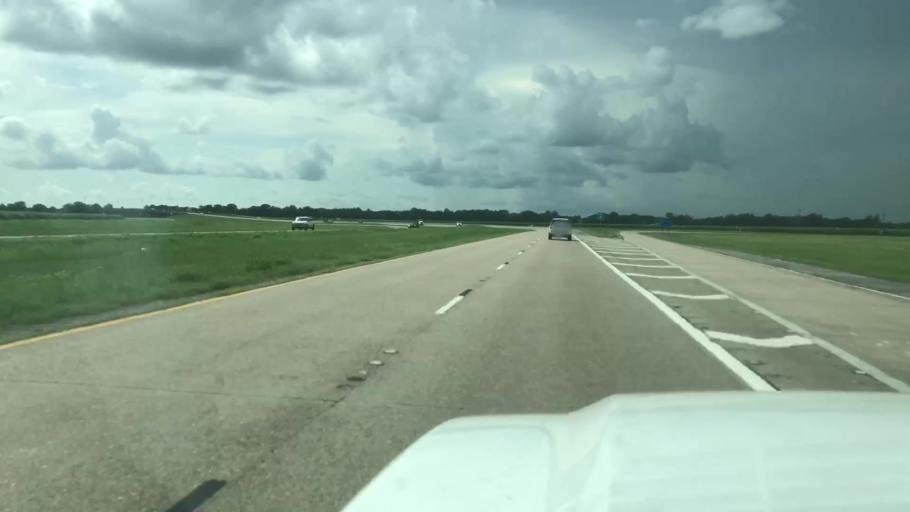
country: US
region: Louisiana
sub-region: Saint Mary Parish
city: Franklin
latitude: 29.7563
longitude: -91.4548
